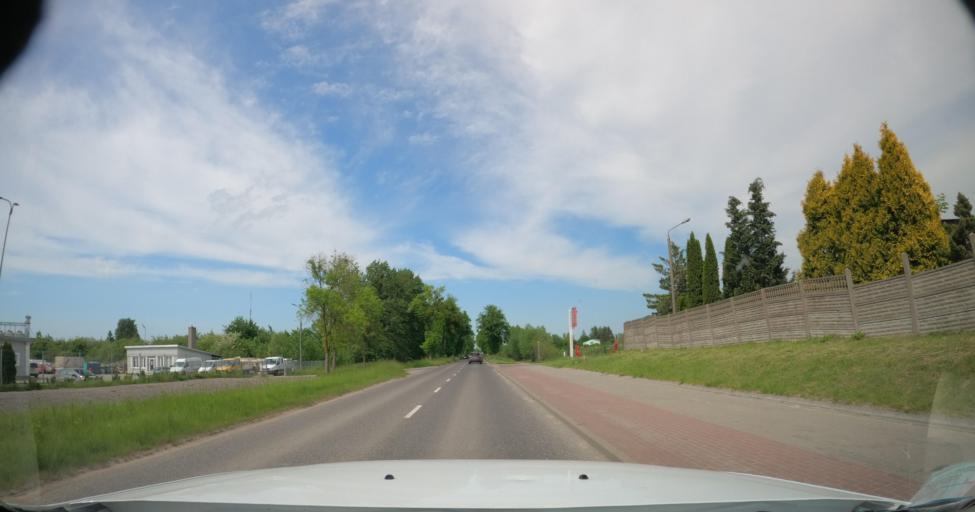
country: PL
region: Warmian-Masurian Voivodeship
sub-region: Powiat lidzbarski
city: Lidzbark Warminski
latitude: 54.1353
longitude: 20.5658
